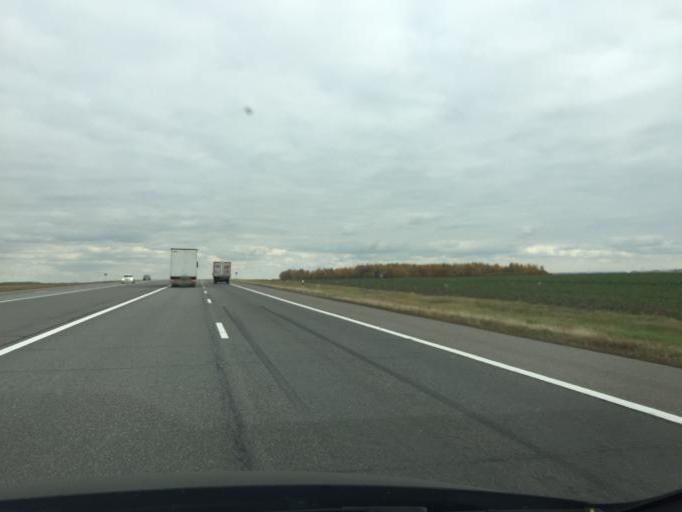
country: BY
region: Minsk
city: Stan'kava
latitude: 53.6808
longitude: 27.2862
